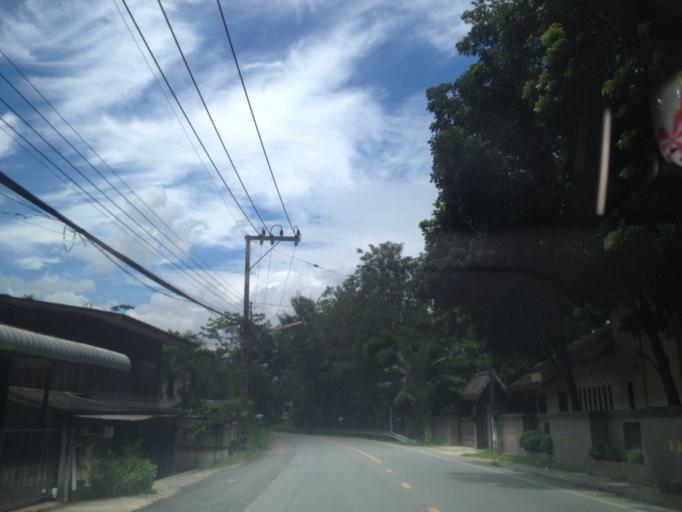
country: TH
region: Chiang Mai
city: Chiang Mai
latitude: 18.7364
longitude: 98.9834
